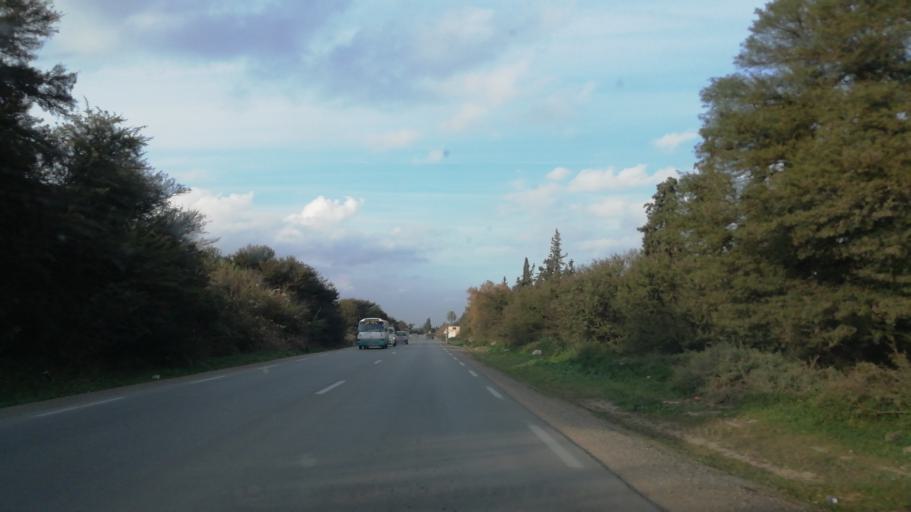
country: DZ
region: Mascara
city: Mascara
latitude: 35.6134
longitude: 0.0518
